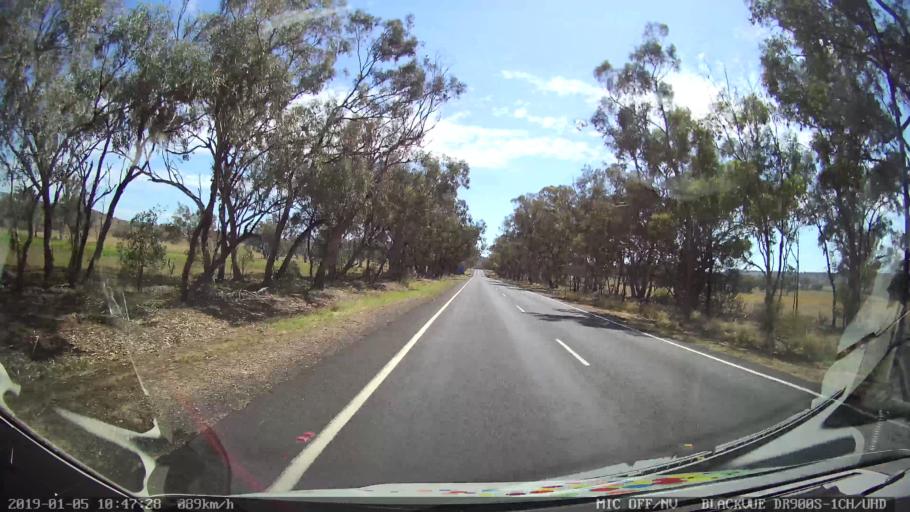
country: AU
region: New South Wales
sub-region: Warrumbungle Shire
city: Coonabarabran
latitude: -31.4447
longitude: 149.0334
